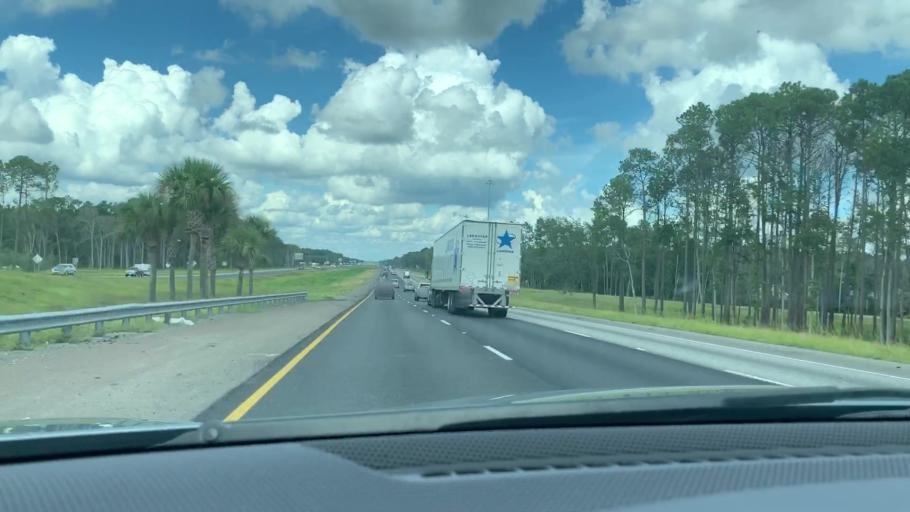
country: US
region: Georgia
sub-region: Camden County
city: Kingsland
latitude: 30.7921
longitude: -81.6590
